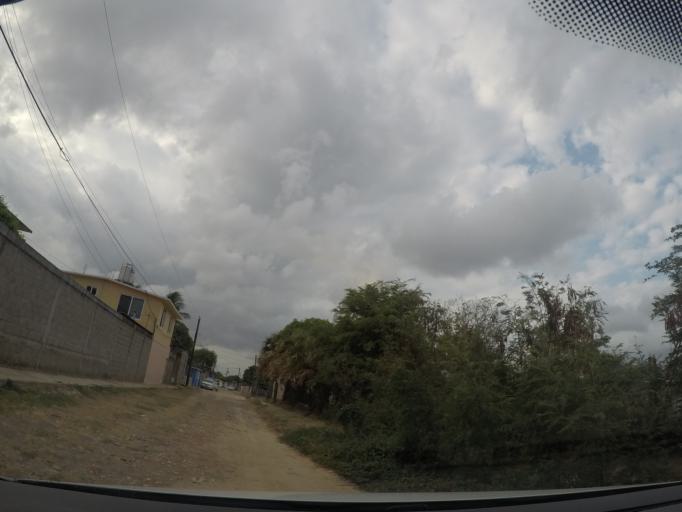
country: MX
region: Oaxaca
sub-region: Salina Cruz
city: Salina Cruz
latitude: 16.2124
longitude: -95.1997
